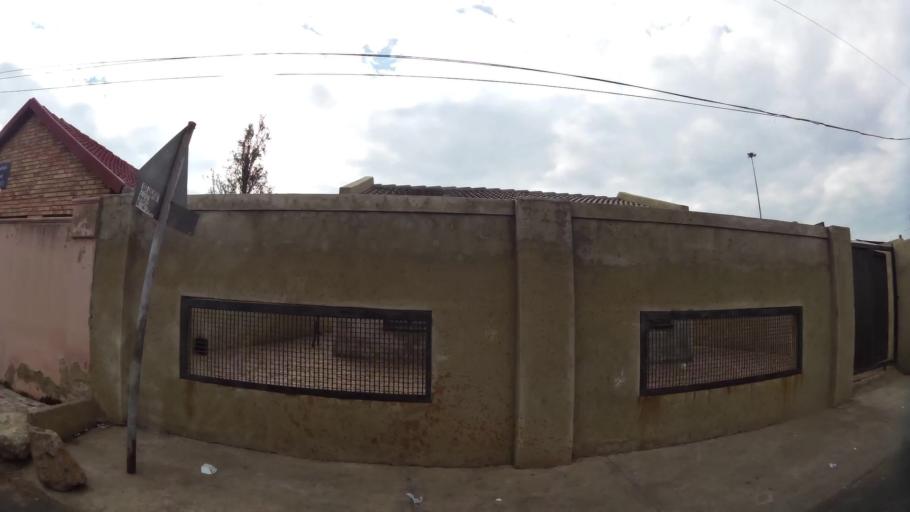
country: ZA
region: Gauteng
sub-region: City of Johannesburg Metropolitan Municipality
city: Soweto
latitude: -26.2352
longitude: 27.8666
